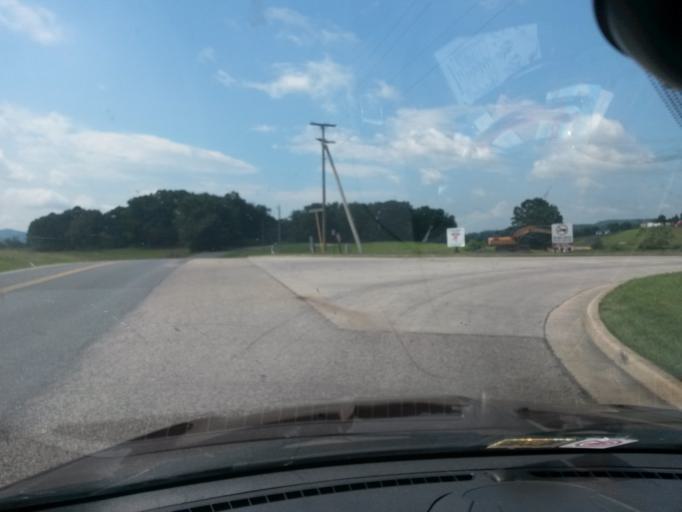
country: US
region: Virginia
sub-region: Augusta County
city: Stuarts Draft
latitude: 37.9270
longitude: -79.2272
